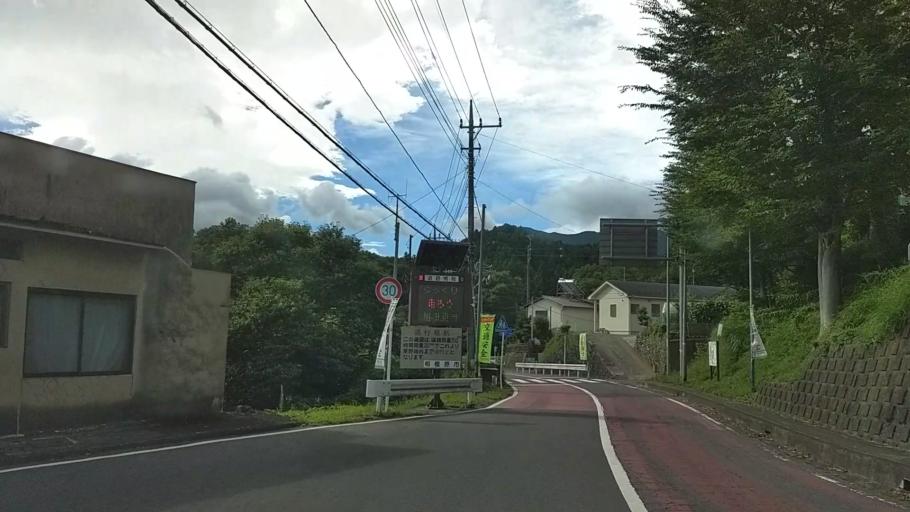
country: JP
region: Yamanashi
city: Uenohara
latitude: 35.5813
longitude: 139.1502
